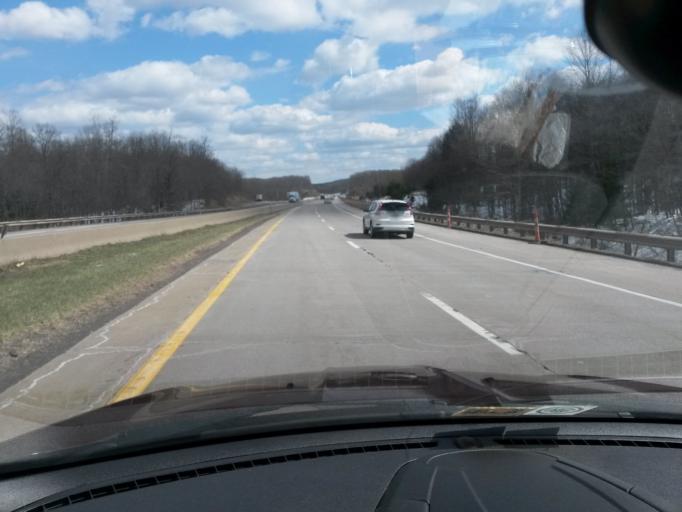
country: US
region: West Virginia
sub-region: Raleigh County
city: Daniels
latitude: 37.7717
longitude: -81.0466
